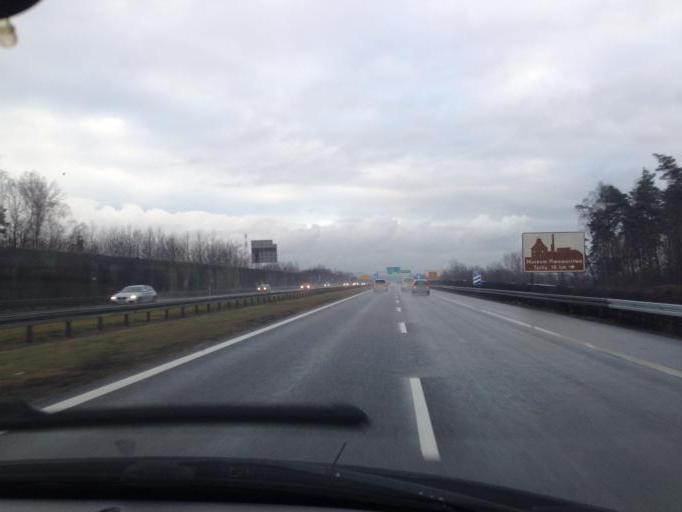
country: PL
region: Silesian Voivodeship
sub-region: Myslowice
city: Myslowice
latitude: 50.2110
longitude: 19.1521
